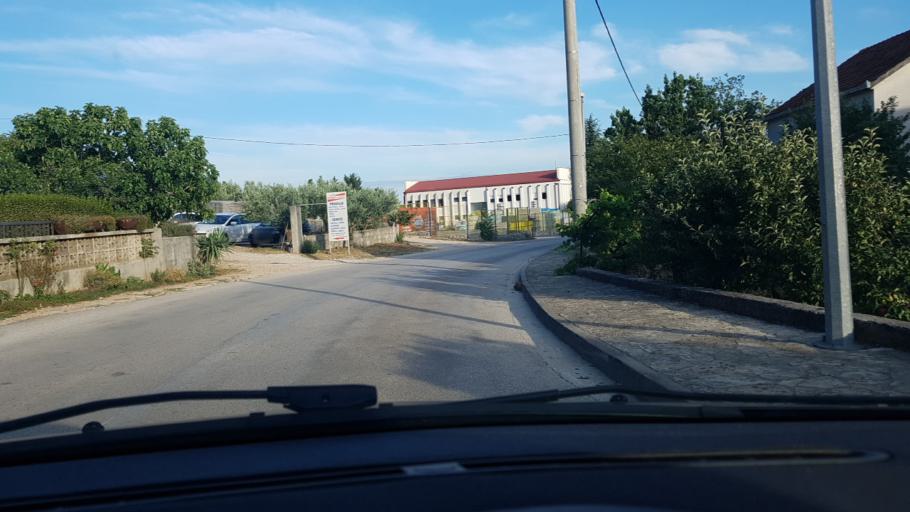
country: HR
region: Splitsko-Dalmatinska
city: Imotski
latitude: 43.4445
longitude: 17.2056
